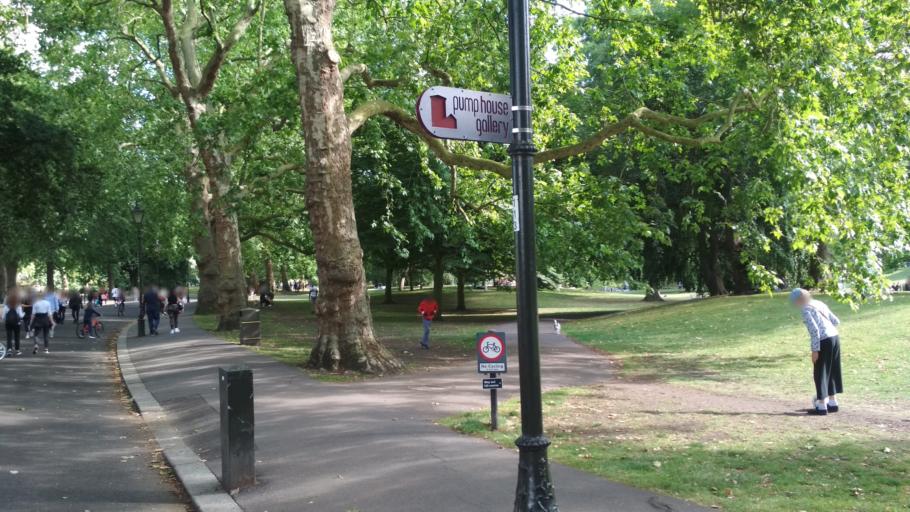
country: GB
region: England
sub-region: Greater London
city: Battersea
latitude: 51.4781
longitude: -0.1633
